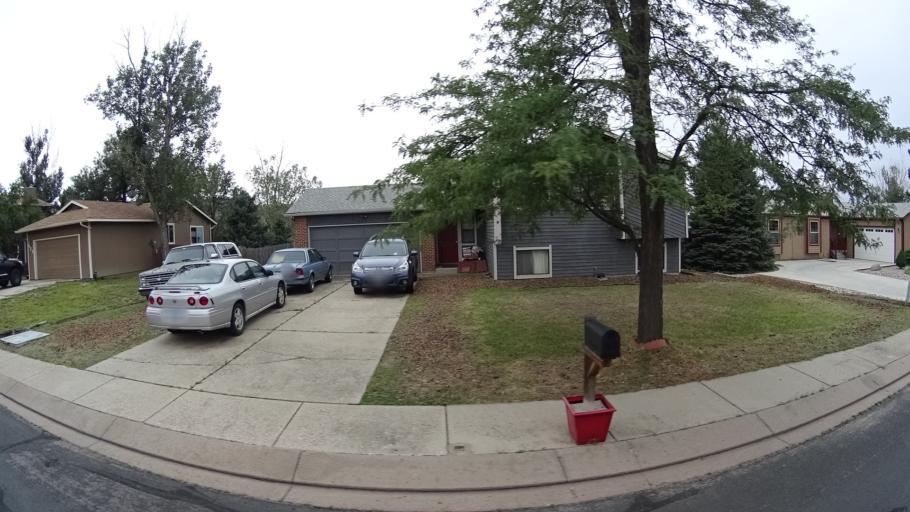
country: US
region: Colorado
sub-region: El Paso County
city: Colorado Springs
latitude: 38.9194
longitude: -104.8118
